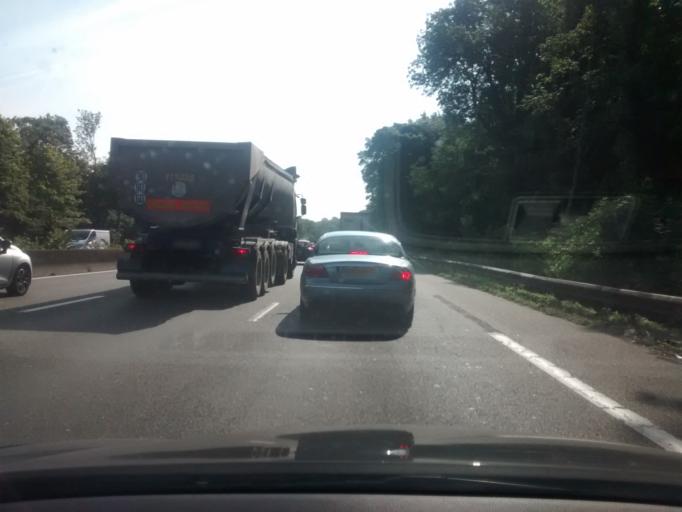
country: FR
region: Ile-de-France
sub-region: Departement des Hauts-de-Seine
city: Marnes-la-Coquette
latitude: 48.8351
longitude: 2.1758
